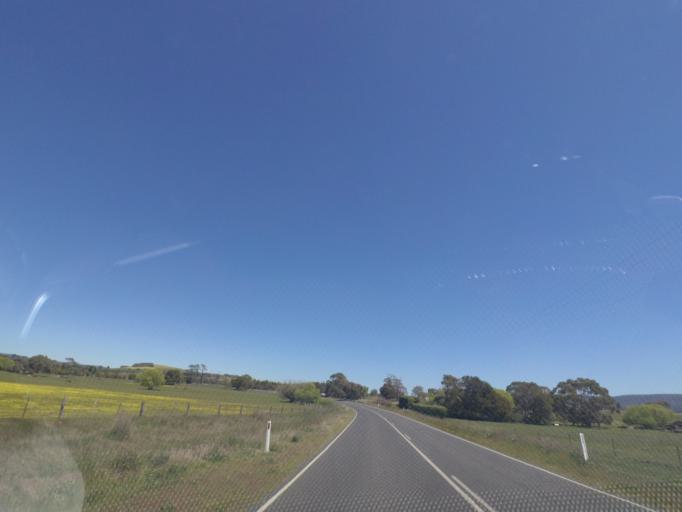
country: AU
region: Victoria
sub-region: Hume
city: Sunbury
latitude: -37.2792
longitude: 144.7160
